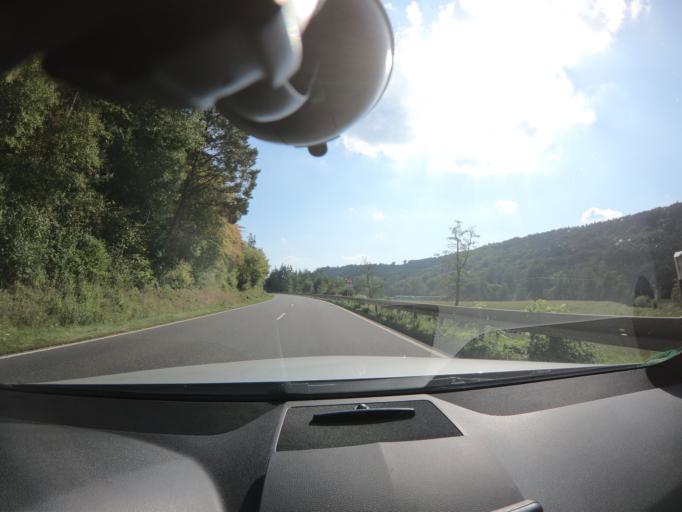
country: DE
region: Hesse
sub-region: Regierungsbezirk Giessen
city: Rauschenberg
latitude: 50.8626
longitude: 8.9310
